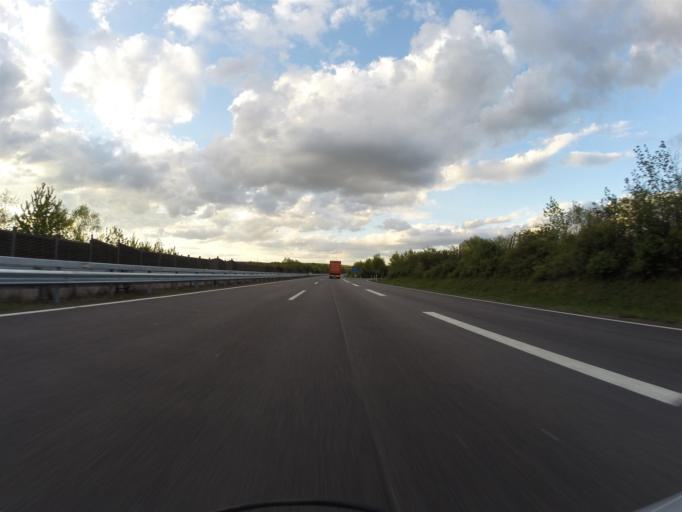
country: DE
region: Rheinland-Pfalz
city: Bischheim
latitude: 49.6658
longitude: 8.0245
